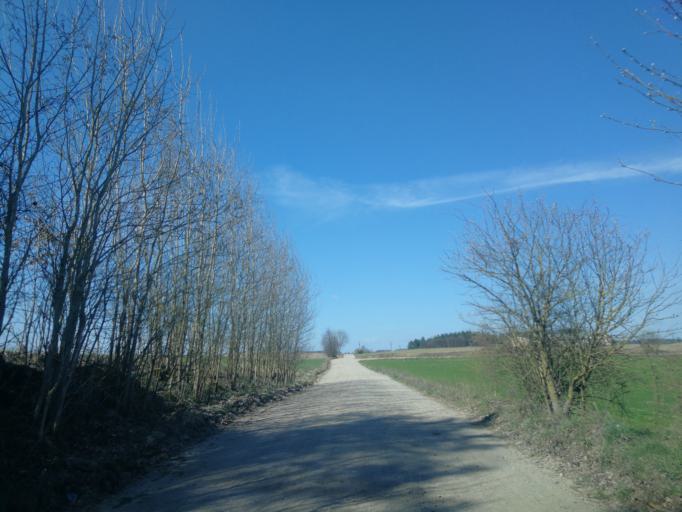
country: PL
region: Warmian-Masurian Voivodeship
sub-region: Powiat dzialdowski
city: Rybno
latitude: 53.4413
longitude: 19.9369
